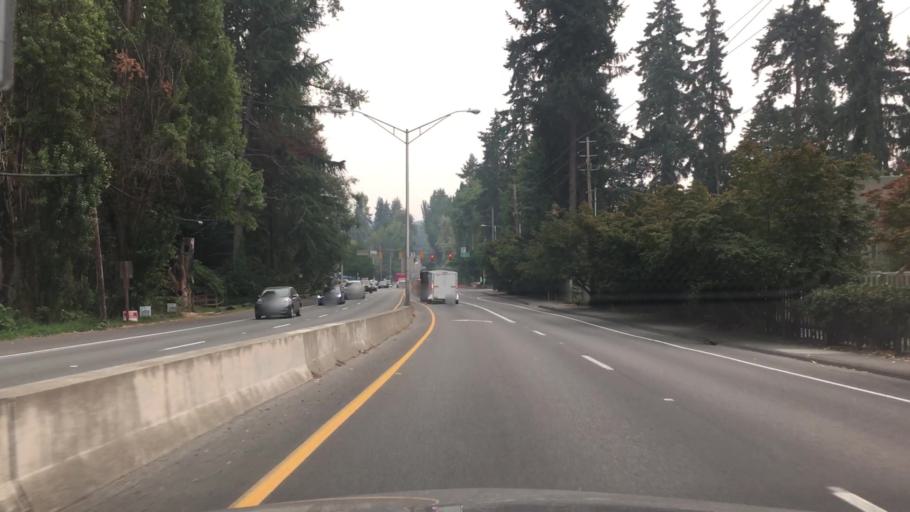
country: US
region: Washington
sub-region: King County
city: Kenmore
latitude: 47.7531
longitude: -122.2500
